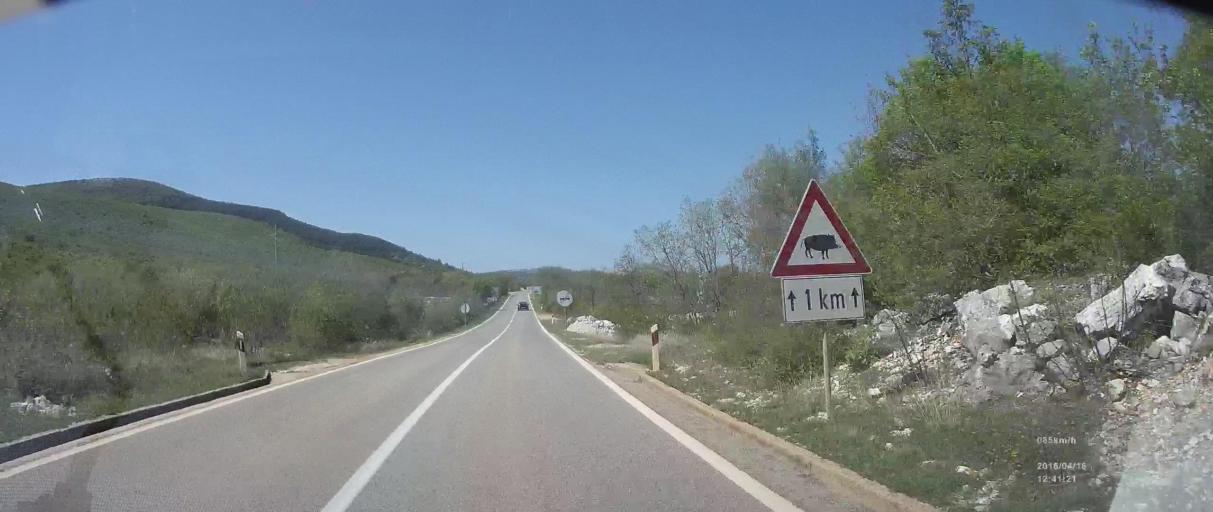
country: HR
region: Sibensko-Kniniska
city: Rogoznica
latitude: 43.6239
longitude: 16.1050
